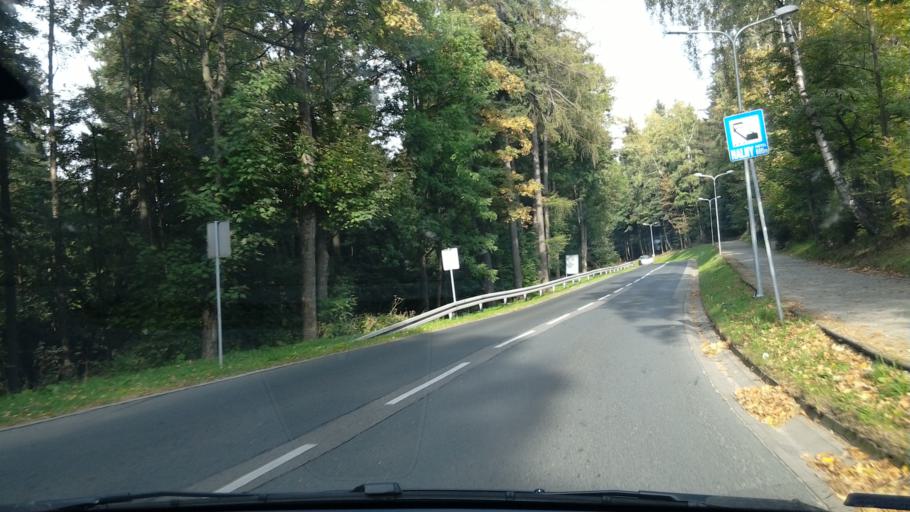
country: PL
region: Lower Silesian Voivodeship
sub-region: Powiat jeleniogorski
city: Karpacz
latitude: 50.7744
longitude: 15.7393
